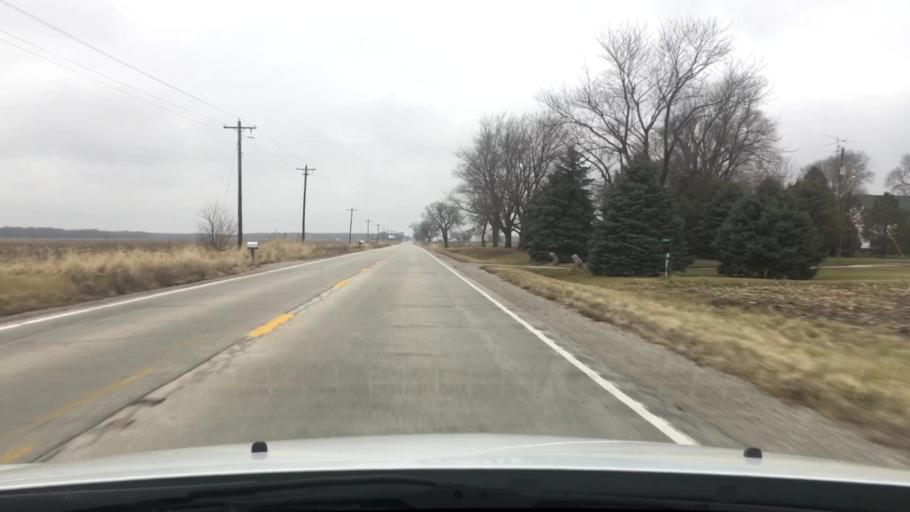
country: US
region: Illinois
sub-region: Iroquois County
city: Watseka
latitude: 40.8887
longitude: -87.7934
